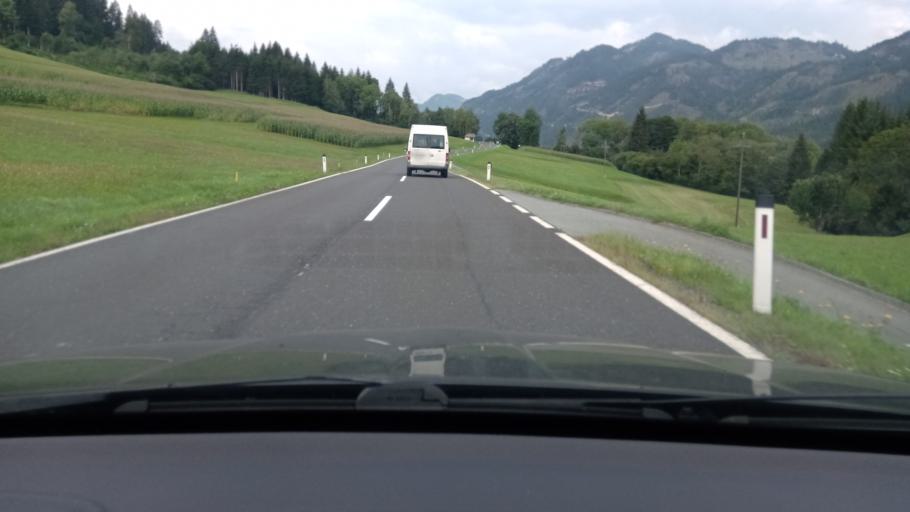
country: AT
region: Carinthia
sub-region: Politischer Bezirk Hermagor
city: Hermagor
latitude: 46.6553
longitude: 13.3216
